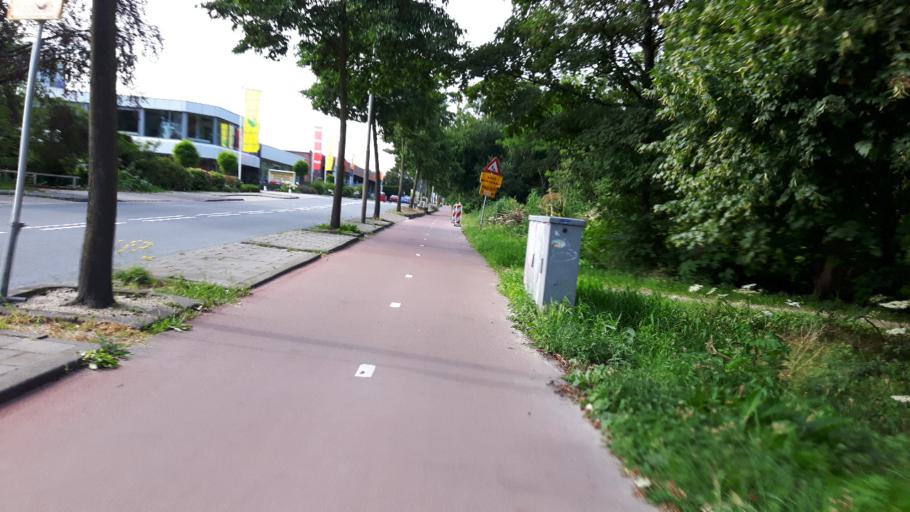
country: NL
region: South Holland
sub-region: Gemeente Delft
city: Delft
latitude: 51.9930
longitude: 4.3725
